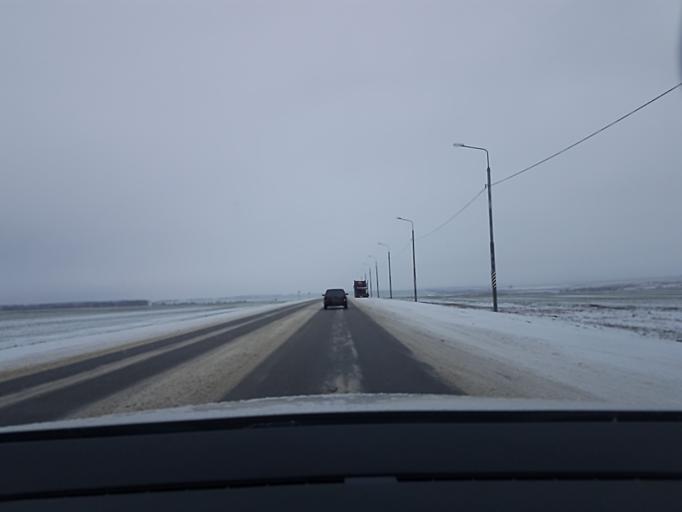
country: RU
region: Rjazan
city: Pavelets
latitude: 54.0007
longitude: 39.3434
